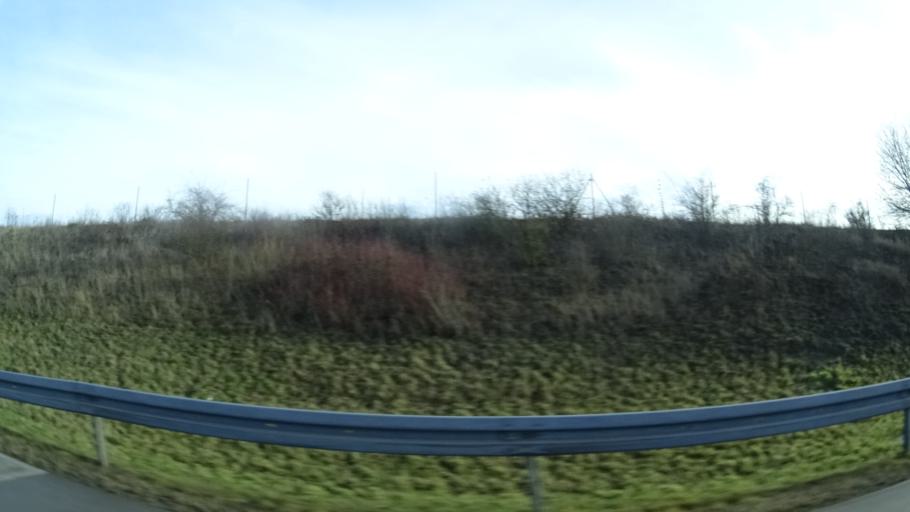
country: DE
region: Bavaria
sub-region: Regierungsbezirk Unterfranken
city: Rodelmaier
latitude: 50.3235
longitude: 10.2888
